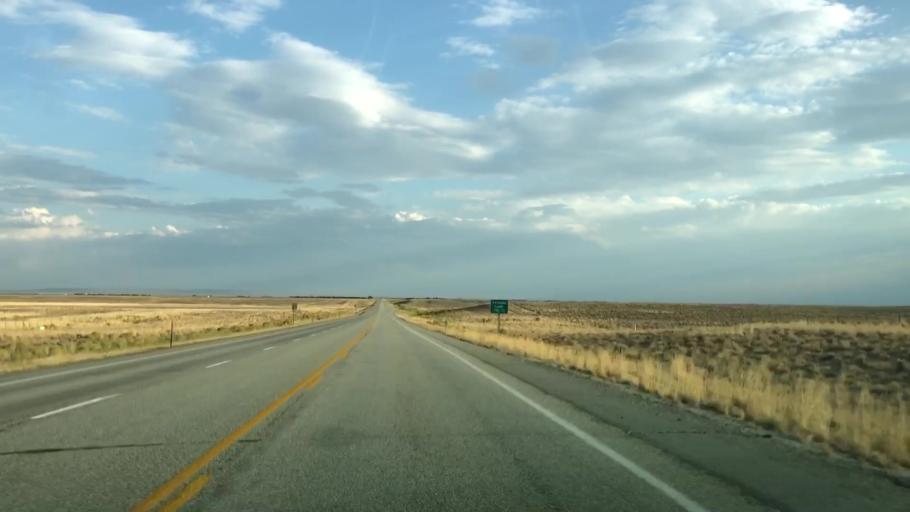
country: US
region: Wyoming
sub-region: Sweetwater County
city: North Rock Springs
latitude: 42.1882
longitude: -109.4800
